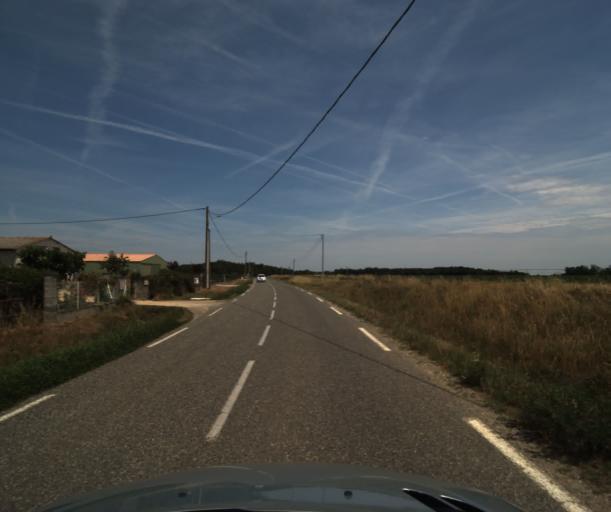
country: FR
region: Midi-Pyrenees
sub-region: Departement de la Haute-Garonne
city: Lherm
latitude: 43.4411
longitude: 1.2272
